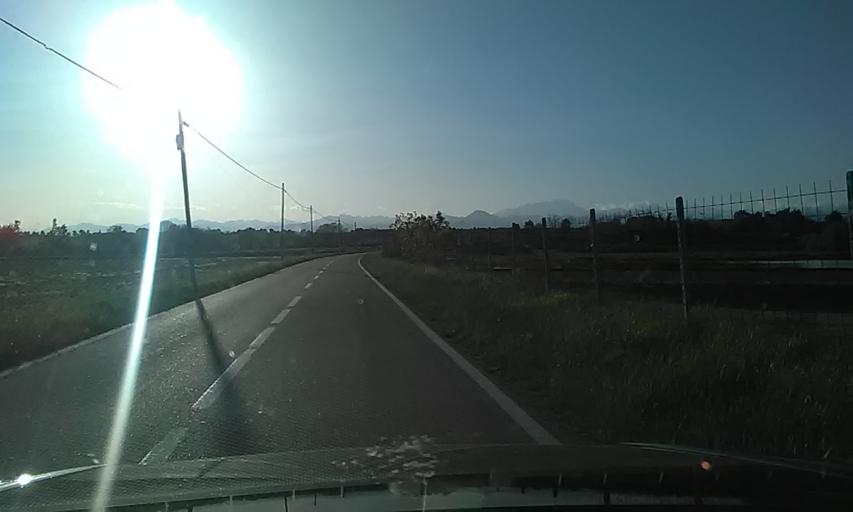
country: IT
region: Piedmont
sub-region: Provincia di Novara
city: Barengo
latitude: 45.5696
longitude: 8.5323
